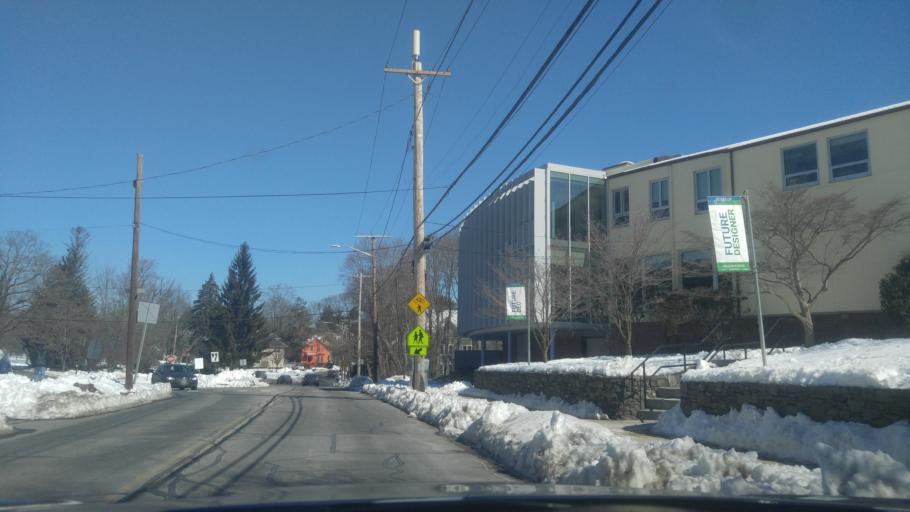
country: US
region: Rhode Island
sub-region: Providence County
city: East Providence
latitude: 41.8328
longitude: -71.3840
